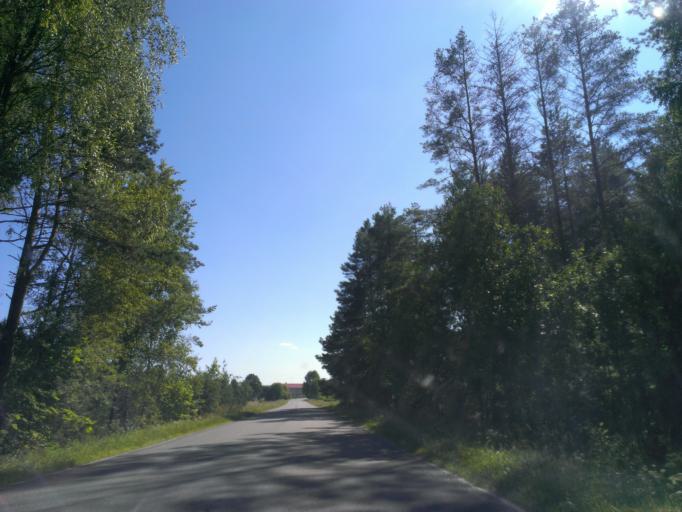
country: LV
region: Sigulda
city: Sigulda
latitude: 57.1062
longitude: 24.8252
